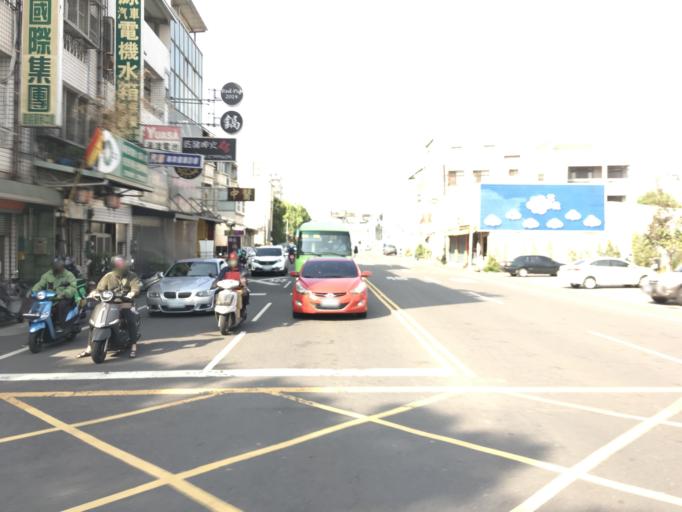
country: TW
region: Taiwan
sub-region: Chiayi
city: Jiayi Shi
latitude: 23.4897
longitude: 120.4592
